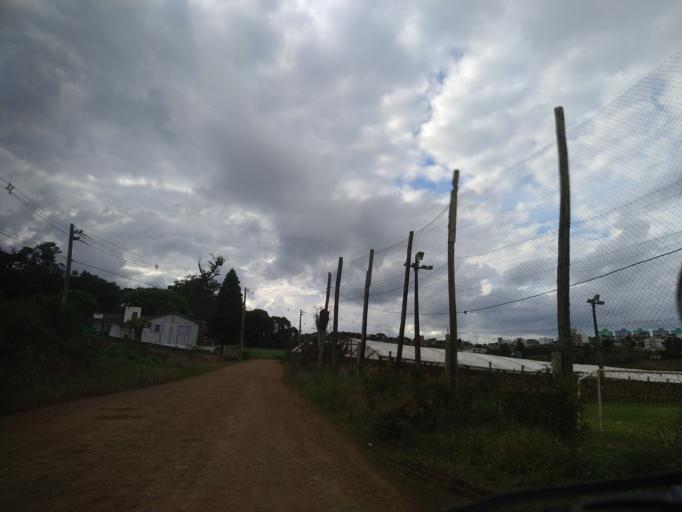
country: BR
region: Santa Catarina
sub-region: Chapeco
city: Chapeco
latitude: -27.0640
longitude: -52.6134
